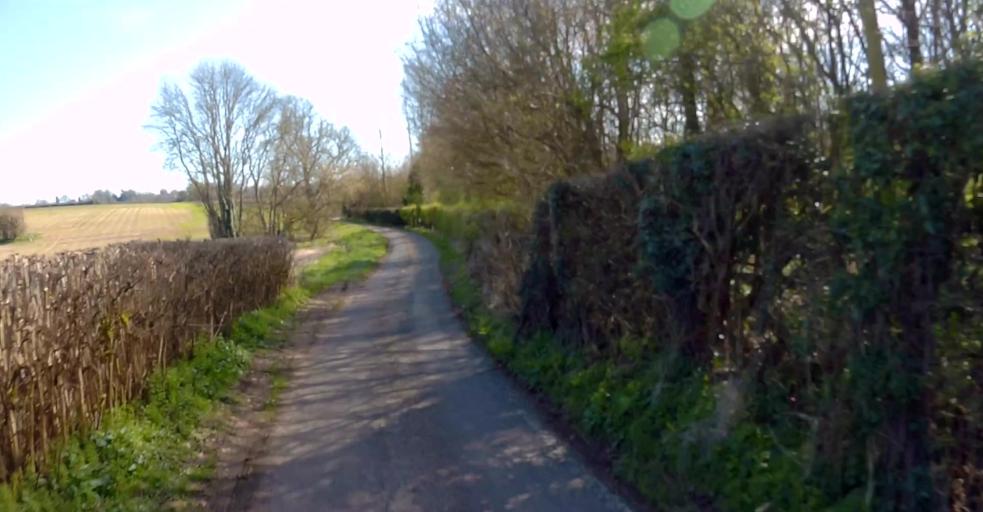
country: GB
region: England
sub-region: Hampshire
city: Four Marks
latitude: 51.1654
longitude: -1.0595
